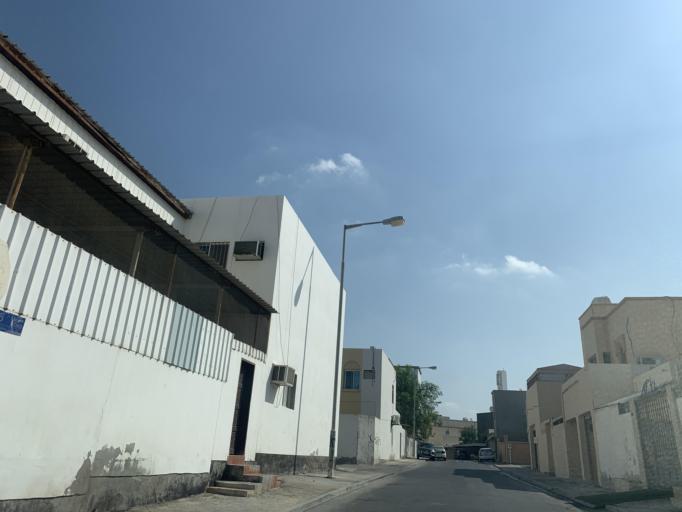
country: BH
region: Central Governorate
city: Madinat Hamad
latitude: 26.1264
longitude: 50.5026
